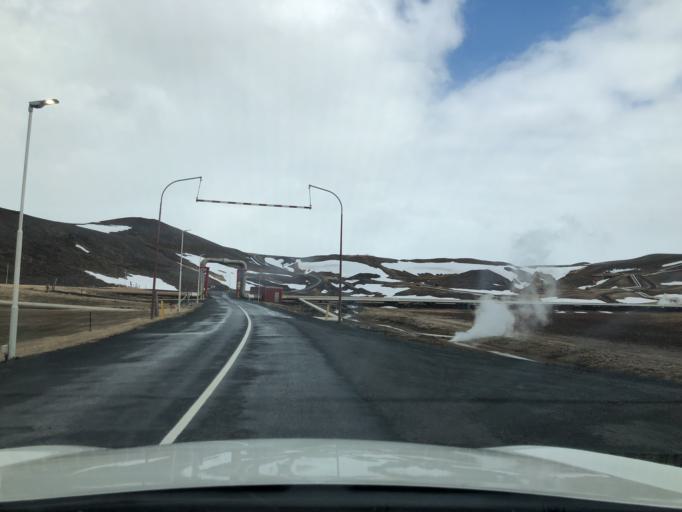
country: IS
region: Northeast
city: Laugar
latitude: 65.7029
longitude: -16.7709
